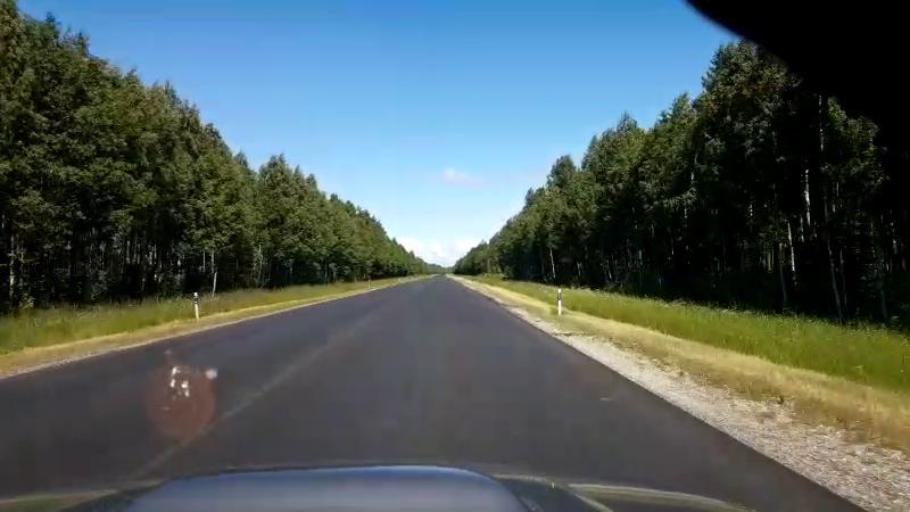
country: LV
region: Salacgrivas
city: Ainazi
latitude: 57.9240
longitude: 24.4240
